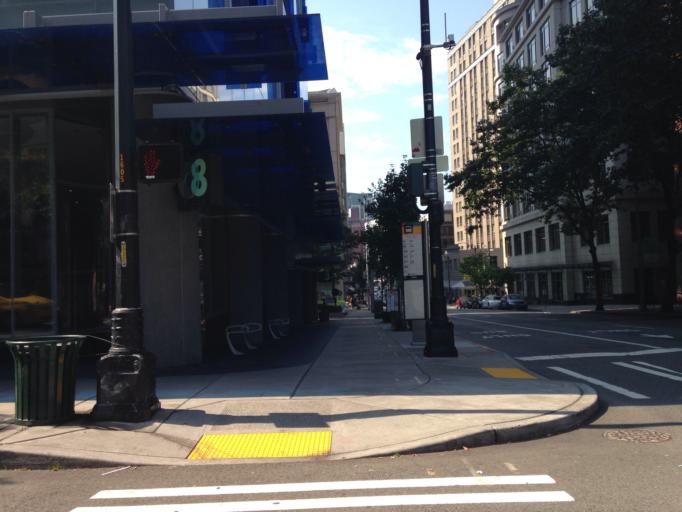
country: US
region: Washington
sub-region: King County
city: Seattle
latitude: 47.6141
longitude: -122.3340
